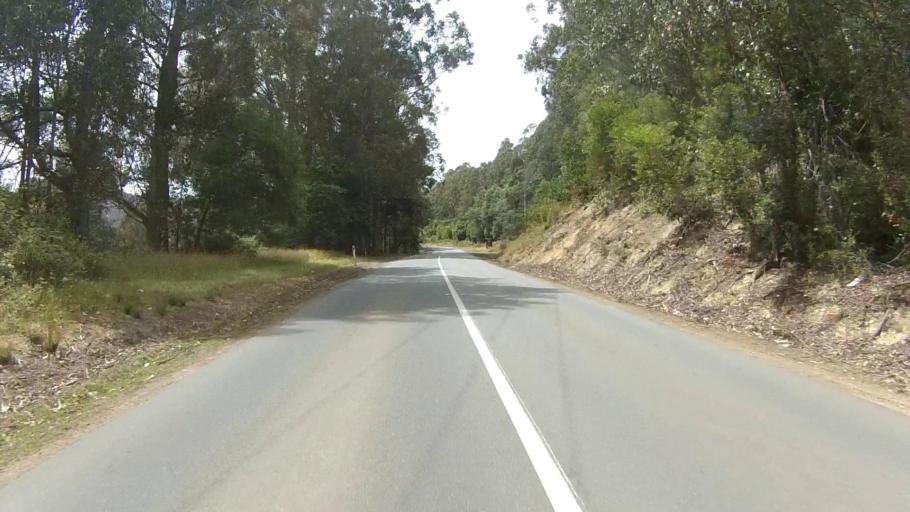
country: AU
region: Tasmania
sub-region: Kingborough
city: Kettering
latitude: -43.1293
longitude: 147.1613
